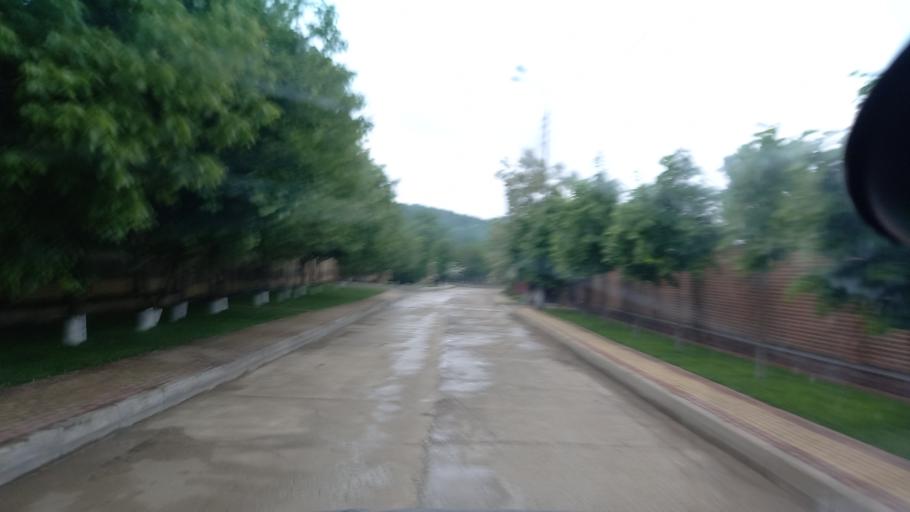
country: RU
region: Krasnodarskiy
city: Azovskaya
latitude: 44.6383
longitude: 38.6171
